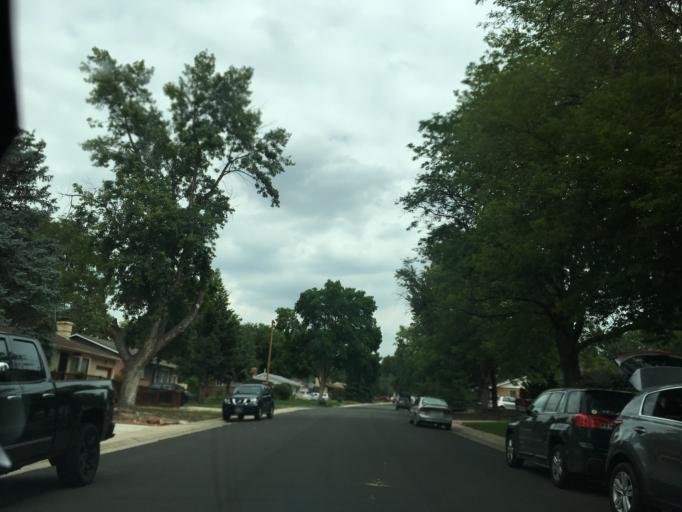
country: US
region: Colorado
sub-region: Arapahoe County
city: Sheridan
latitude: 39.6591
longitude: -105.0498
